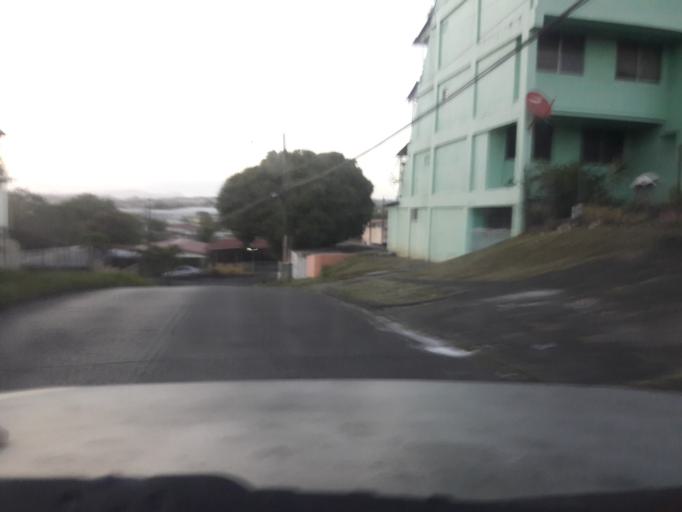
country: PA
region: Panama
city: San Miguelito
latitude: 9.0533
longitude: -79.4353
